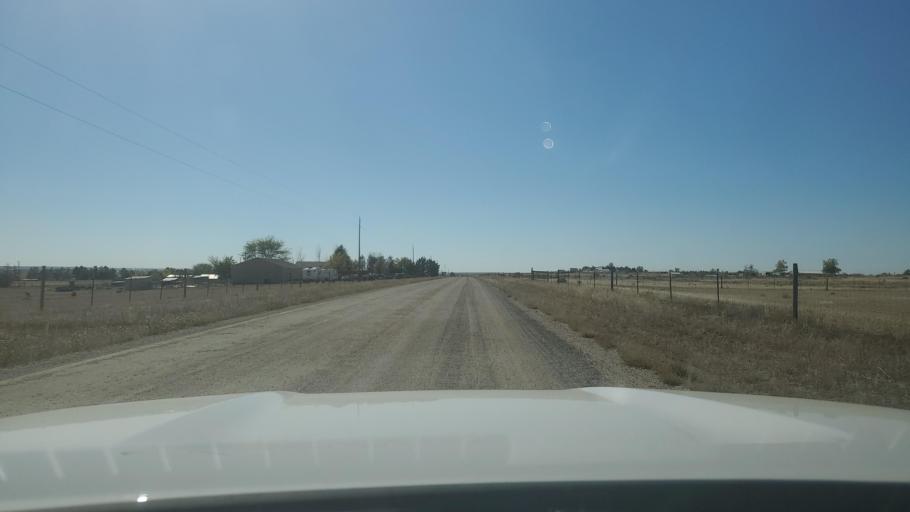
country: US
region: Colorado
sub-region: Adams County
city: Bennett
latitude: 39.7742
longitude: -104.3768
